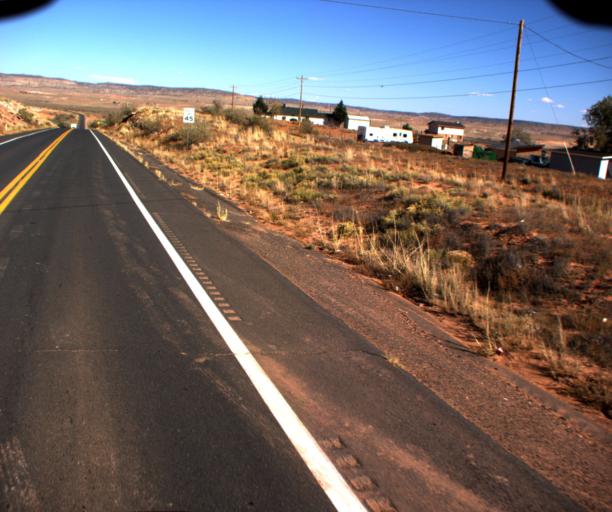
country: US
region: Arizona
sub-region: Coconino County
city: Kaibito
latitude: 36.3202
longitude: -110.9445
